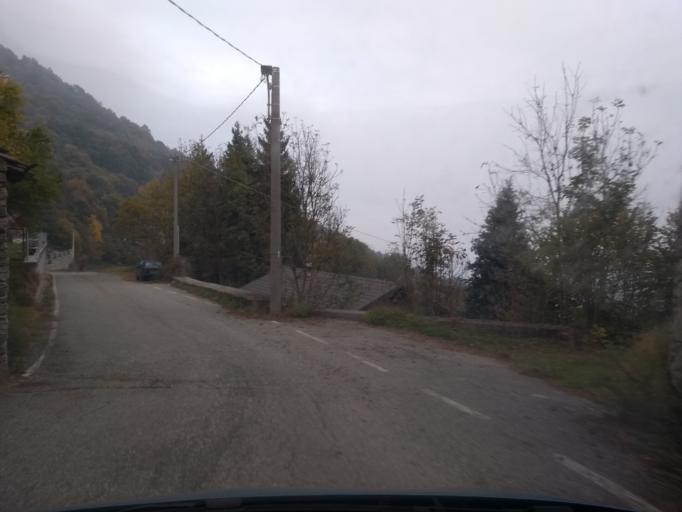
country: IT
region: Piedmont
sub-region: Provincia di Torino
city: Pessinetto
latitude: 45.3024
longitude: 7.4132
